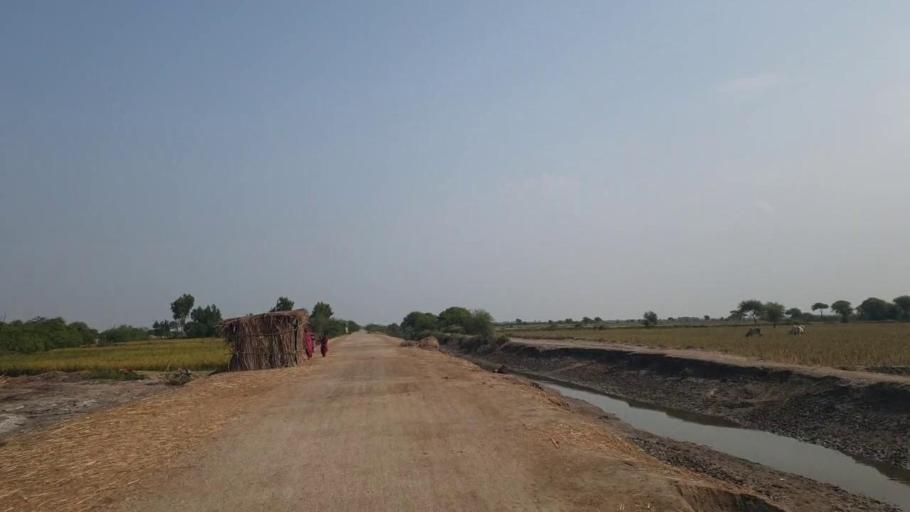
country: PK
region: Sindh
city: Badin
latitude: 24.7560
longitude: 68.7649
